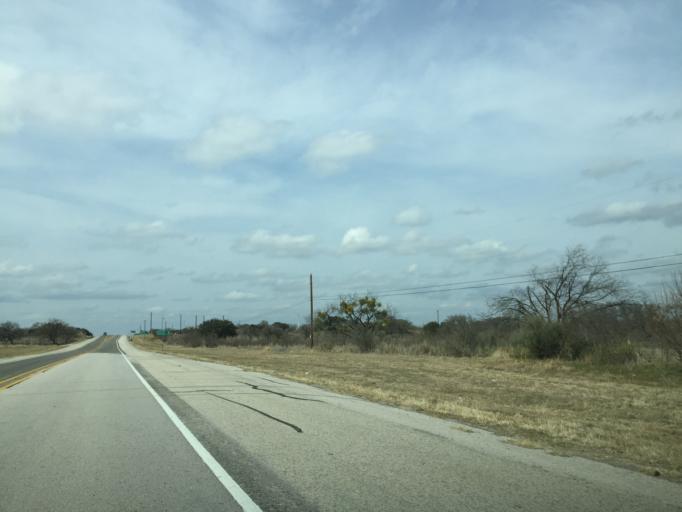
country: US
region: Texas
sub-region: Llano County
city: Horseshoe Bay
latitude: 30.5176
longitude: -98.4055
